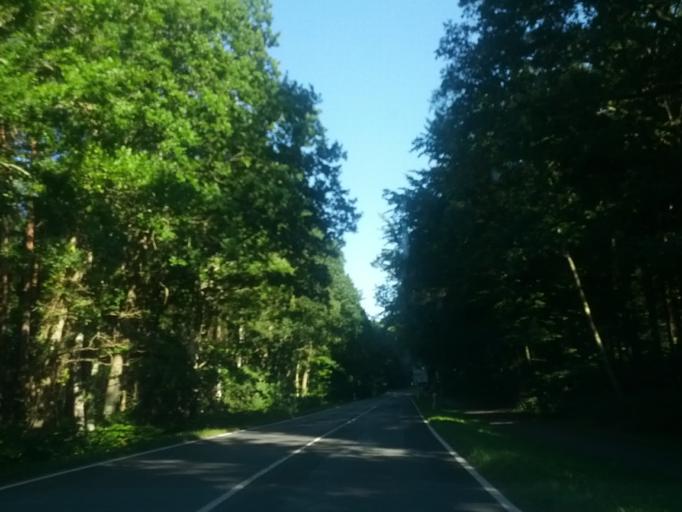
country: DE
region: Mecklenburg-Vorpommern
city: Ostseebad Gohren
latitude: 54.3438
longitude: 13.7171
